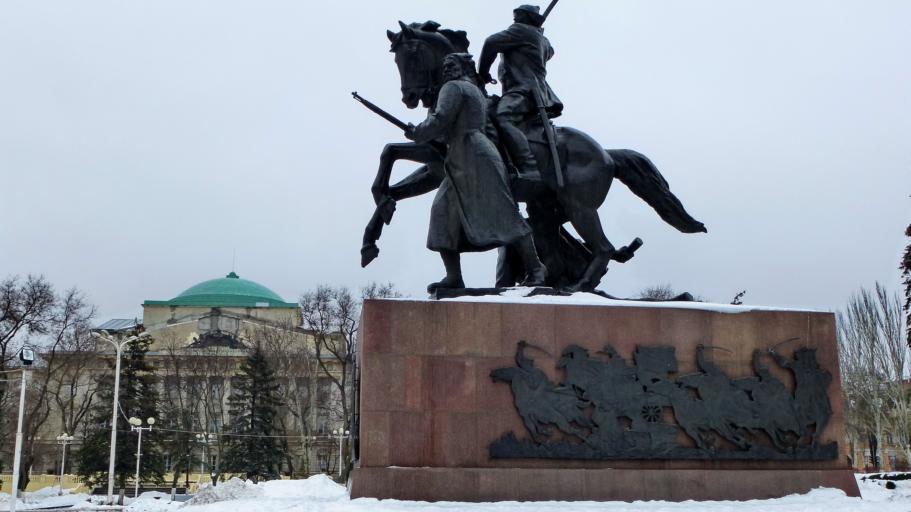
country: RU
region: Rostov
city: Rostov-na-Donu
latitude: 47.2219
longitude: 39.7196
